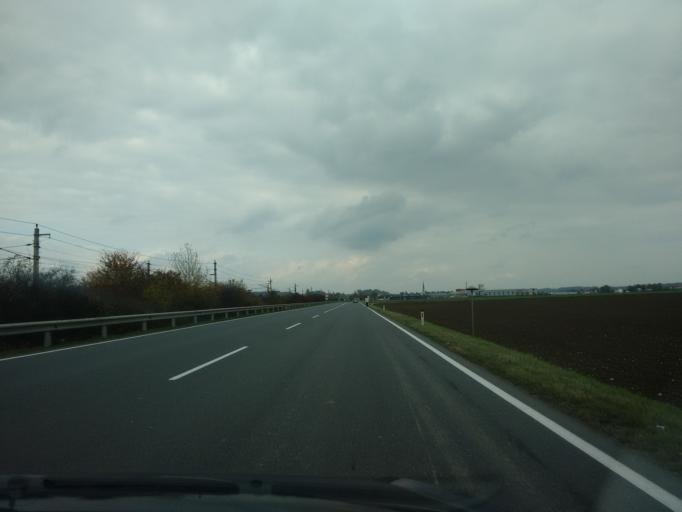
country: AT
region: Upper Austria
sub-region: Politischer Bezirk Vocklabruck
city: Oberndorf bei Schwanenstadt
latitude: 48.0413
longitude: 13.7496
